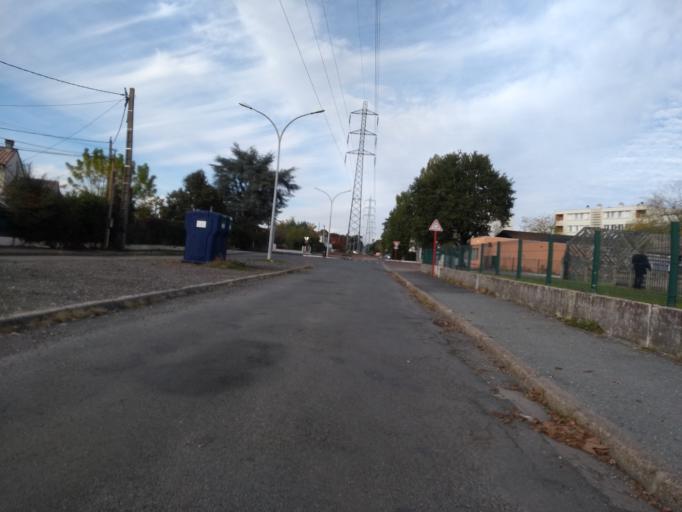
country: FR
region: Aquitaine
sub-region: Departement de la Gironde
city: Pessac
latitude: 44.7977
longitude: -0.6757
